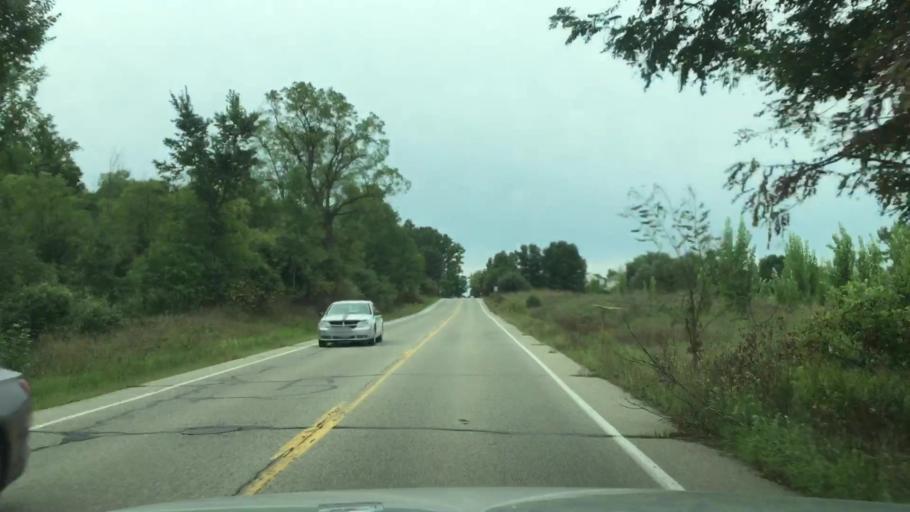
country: US
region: Michigan
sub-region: Washtenaw County
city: Ypsilanti
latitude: 42.2105
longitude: -83.6600
